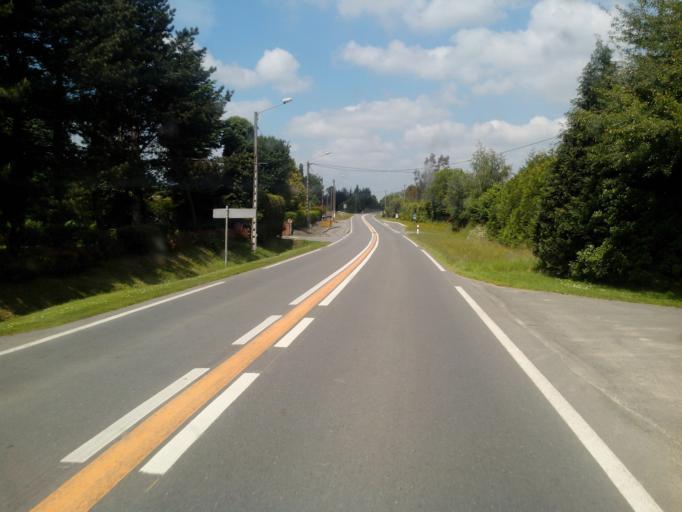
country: FR
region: Brittany
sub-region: Departement d'Ille-et-Vilaine
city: Lecousse
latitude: 48.3718
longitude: -1.2427
